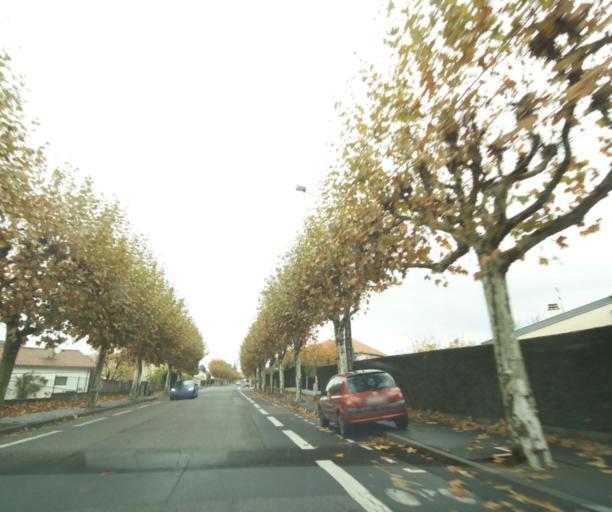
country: FR
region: Auvergne
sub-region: Departement du Puy-de-Dome
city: Cournon-d'Auvergne
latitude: 45.7341
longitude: 3.1898
